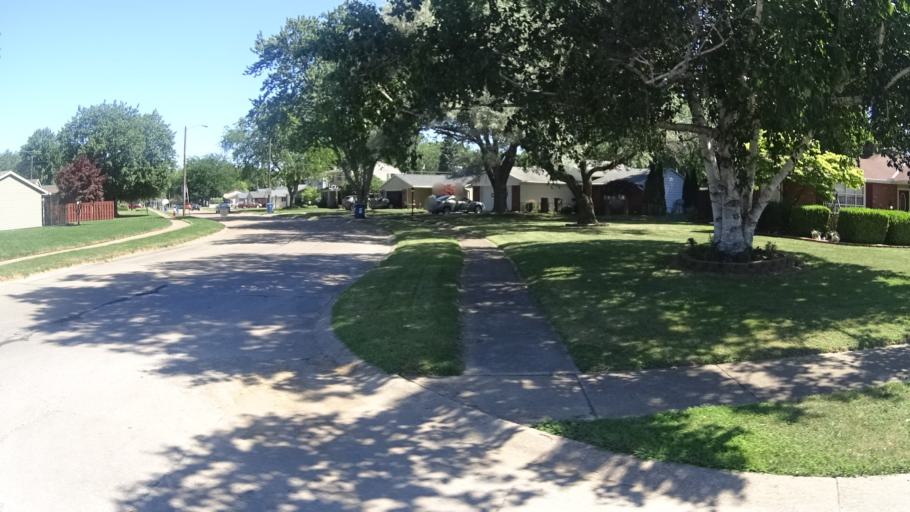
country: US
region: Ohio
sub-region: Erie County
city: Sandusky
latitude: 41.4249
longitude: -82.6543
